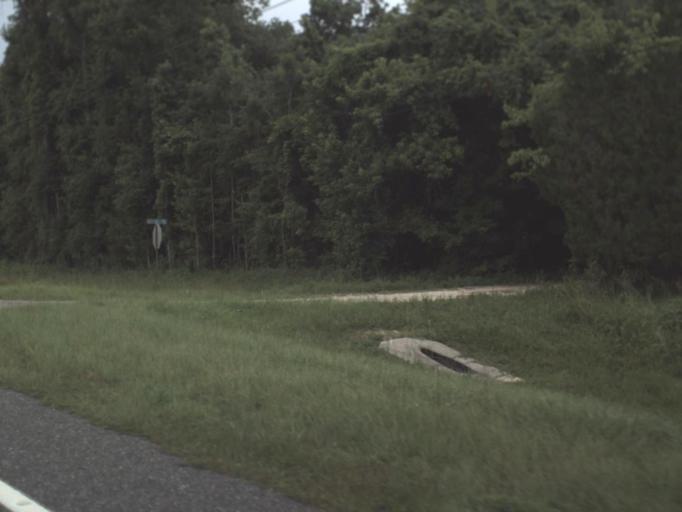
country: US
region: Florida
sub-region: Levy County
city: Williston Highlands
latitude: 29.2409
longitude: -82.7159
